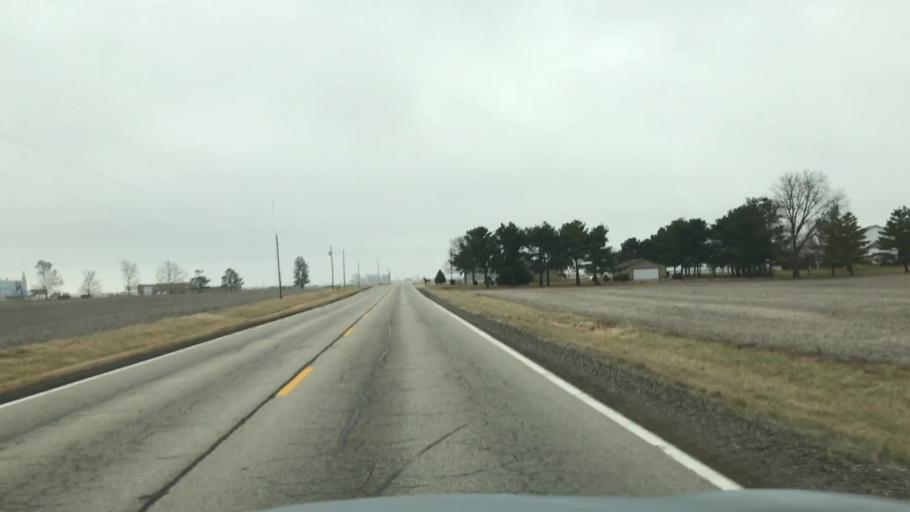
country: US
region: Illinois
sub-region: McLean County
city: Hudson
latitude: 40.5873
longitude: -88.9448
